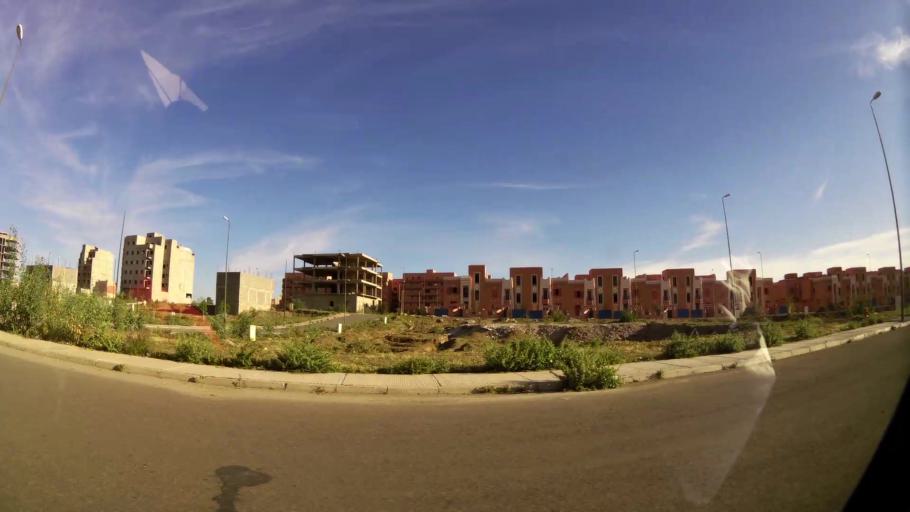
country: MA
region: Marrakech-Tensift-Al Haouz
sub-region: Marrakech
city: Marrakesh
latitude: 31.7556
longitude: -8.1031
